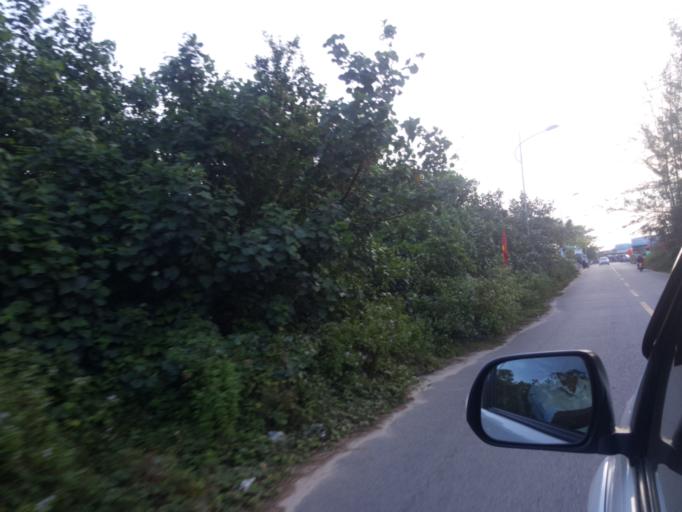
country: VN
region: Kien Giang
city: Duong GJong
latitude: 10.1494
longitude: 104.0354
